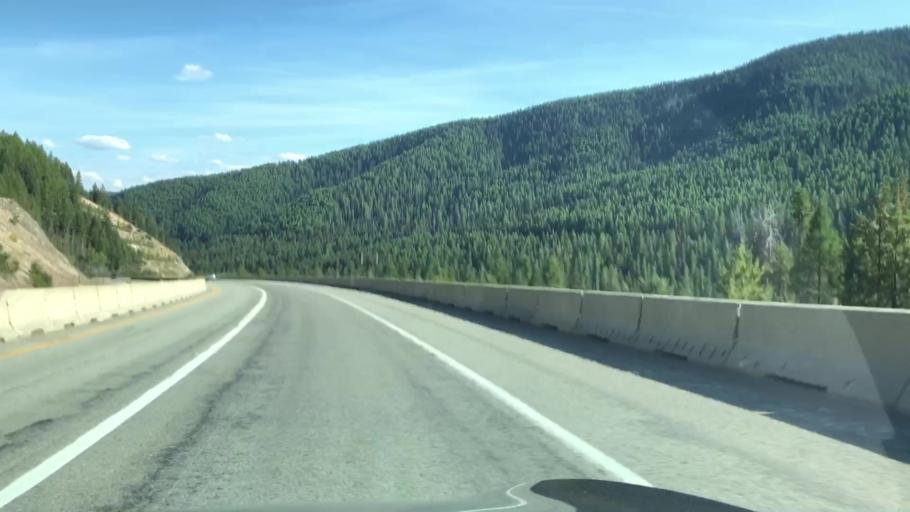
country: US
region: Idaho
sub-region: Shoshone County
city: Wallace
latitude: 47.4424
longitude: -115.6897
